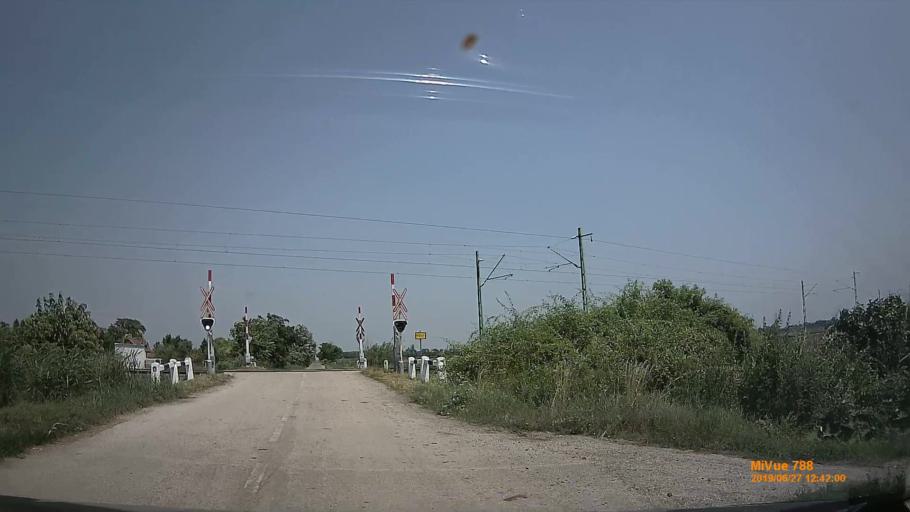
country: HU
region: Pest
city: Tortel
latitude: 47.1824
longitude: 19.8935
